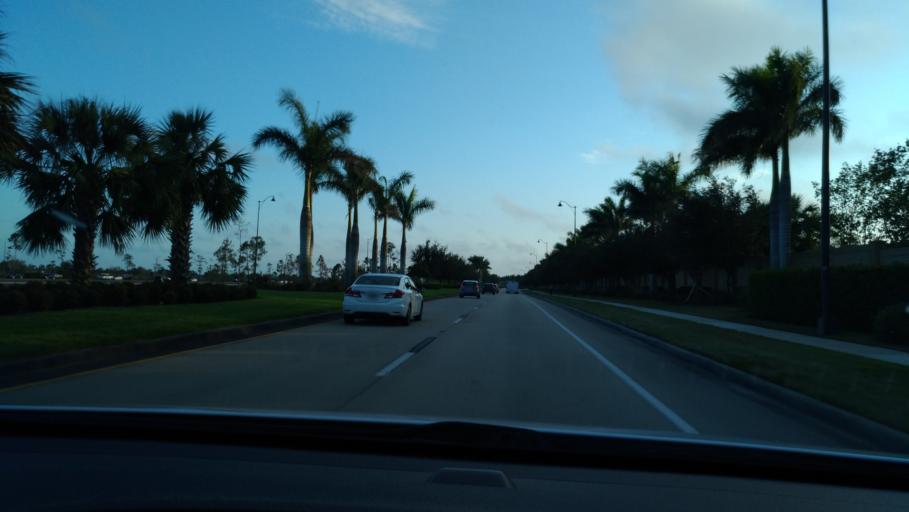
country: US
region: Florida
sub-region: Lee County
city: Bonita Springs
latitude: 26.3824
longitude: -81.7734
